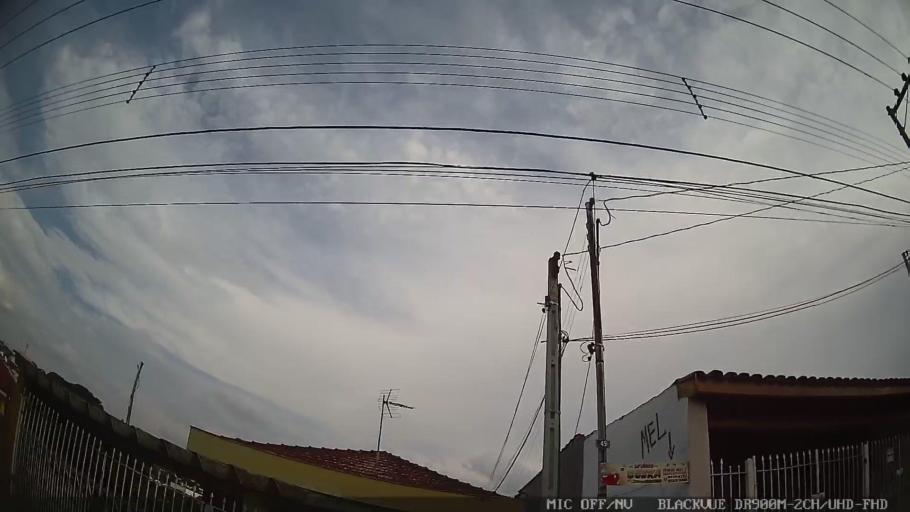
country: BR
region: Sao Paulo
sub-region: Braganca Paulista
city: Braganca Paulista
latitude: -22.9453
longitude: -46.5430
